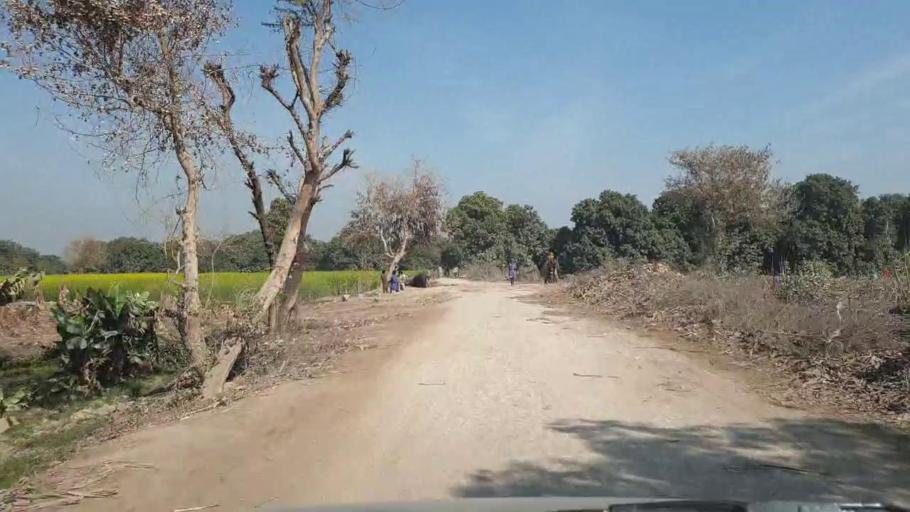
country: PK
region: Sindh
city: Chambar
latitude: 25.3854
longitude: 68.7806
